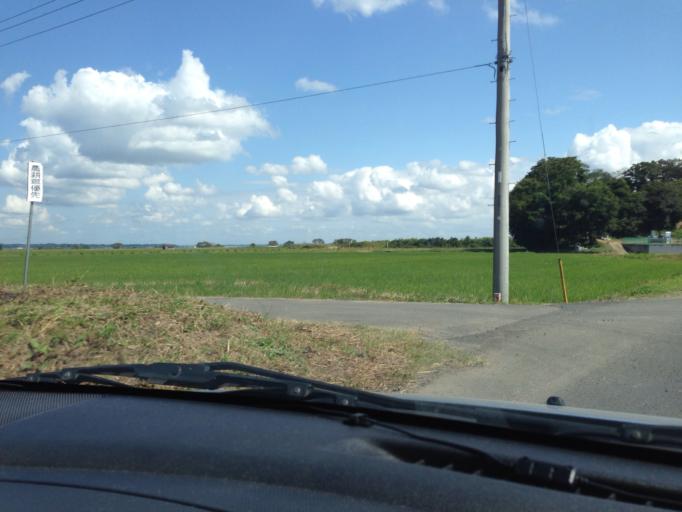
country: JP
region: Ibaraki
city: Inashiki
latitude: 36.0240
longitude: 140.3144
